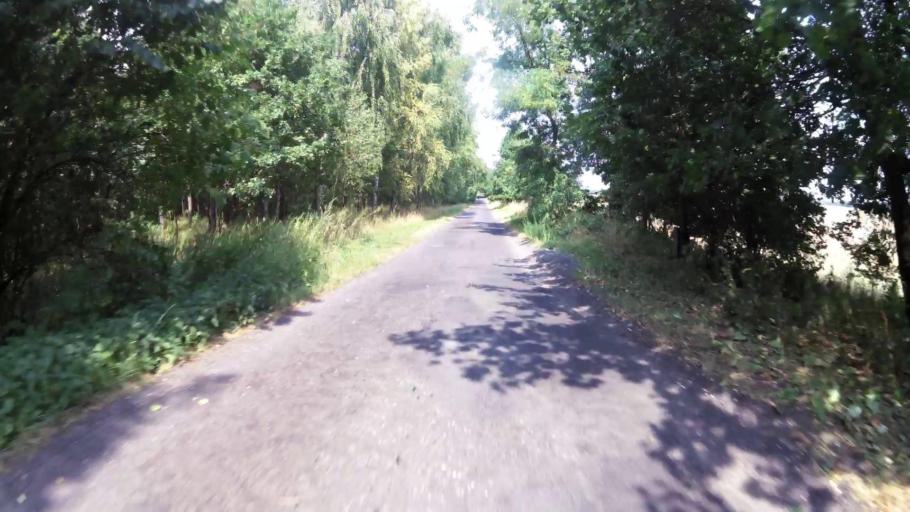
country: PL
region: West Pomeranian Voivodeship
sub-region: Powiat gryfinski
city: Mieszkowice
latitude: 52.8556
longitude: 14.5260
